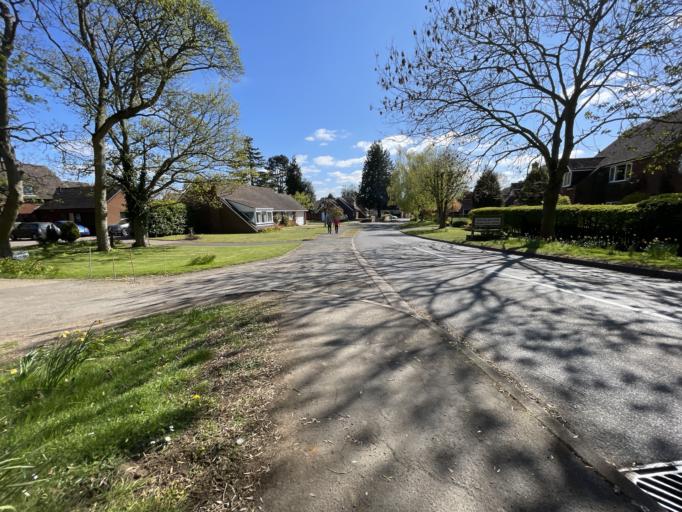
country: GB
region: England
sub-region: Warwickshire
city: Dunchurch
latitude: 52.3376
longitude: -1.3134
